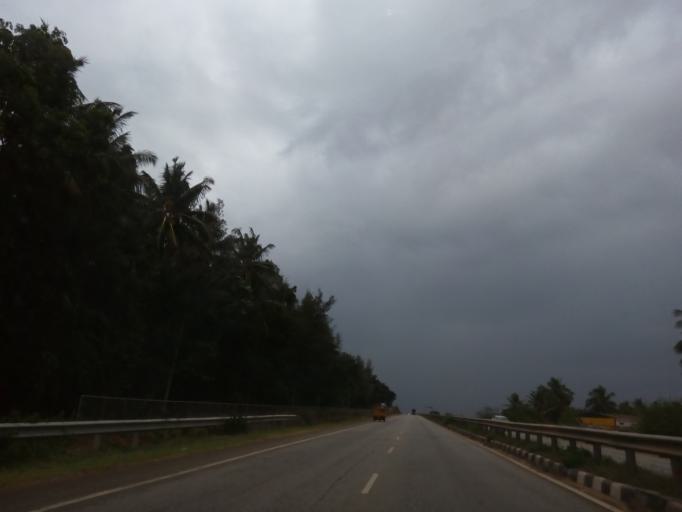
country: IN
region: Karnataka
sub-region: Davanagere
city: Harihar
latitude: 14.4626
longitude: 75.8509
